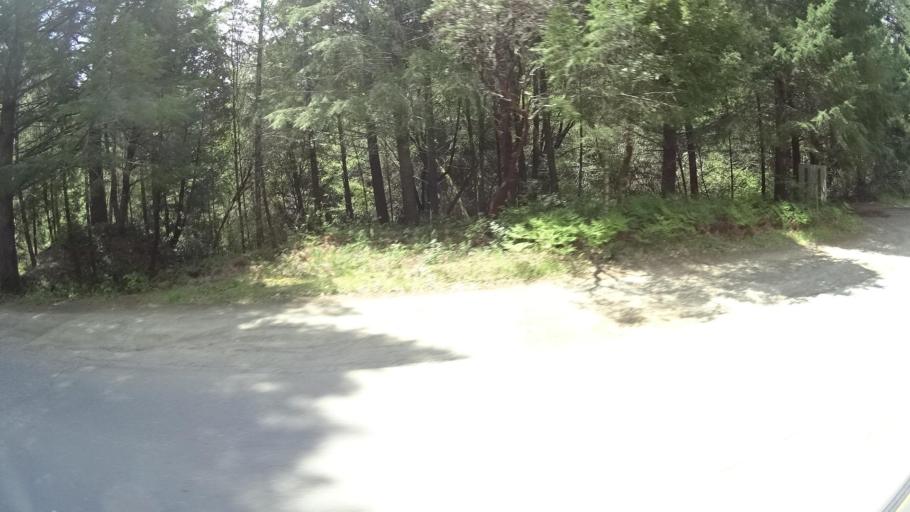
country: US
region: California
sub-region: Humboldt County
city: Redway
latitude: 40.0607
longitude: -123.9600
